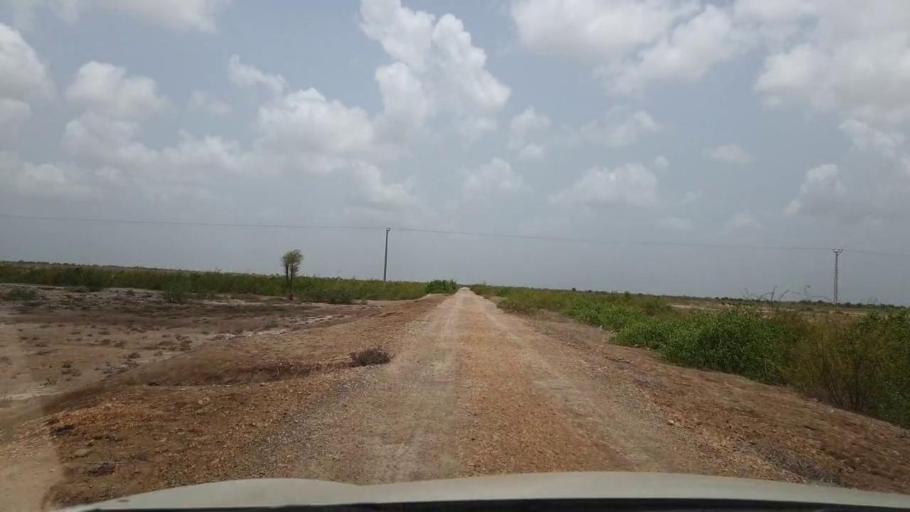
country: PK
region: Sindh
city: Chambar
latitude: 25.2225
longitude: 68.7595
